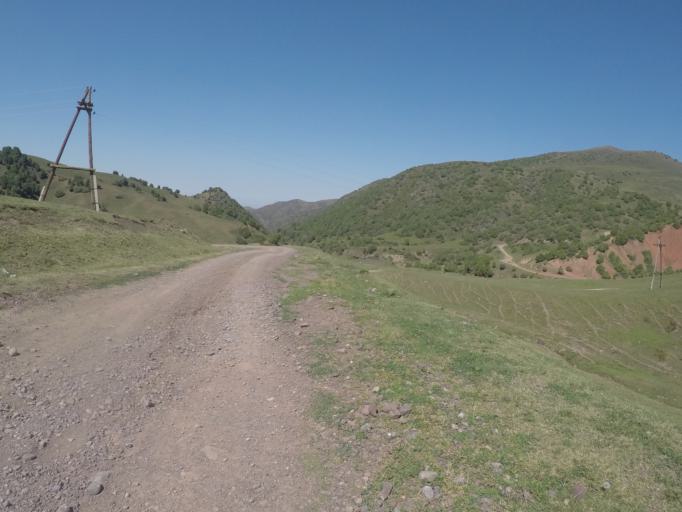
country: KG
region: Chuy
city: Bishkek
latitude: 42.6452
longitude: 74.5742
